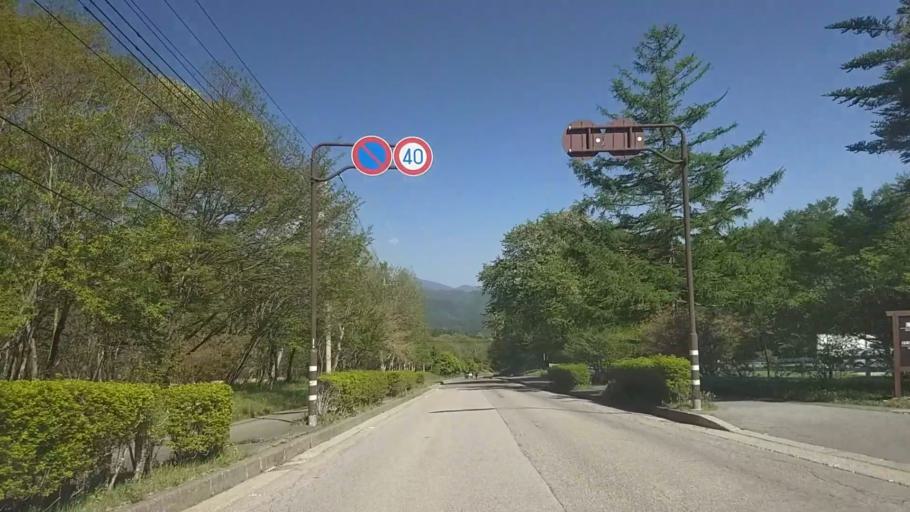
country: JP
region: Yamanashi
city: Nirasaki
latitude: 35.9219
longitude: 138.4289
